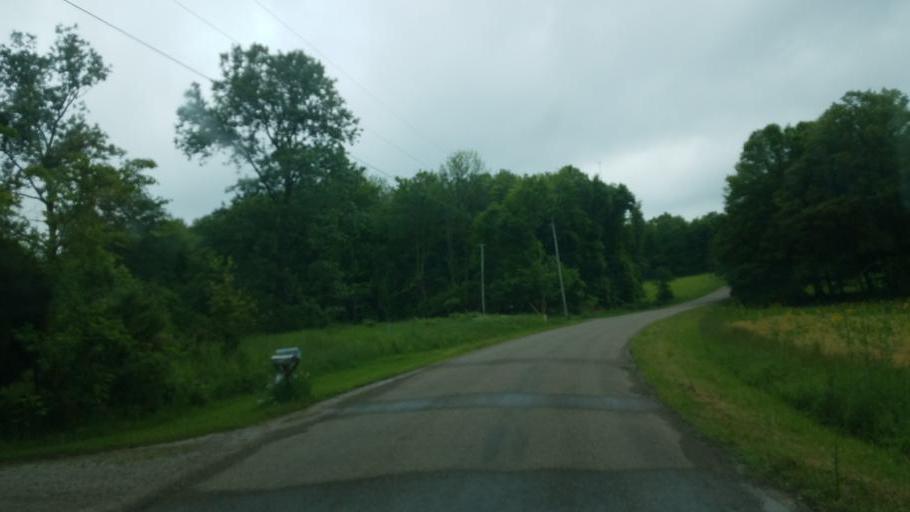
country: US
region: Ohio
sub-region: Richland County
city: Lincoln Heights
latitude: 40.7502
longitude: -82.4295
